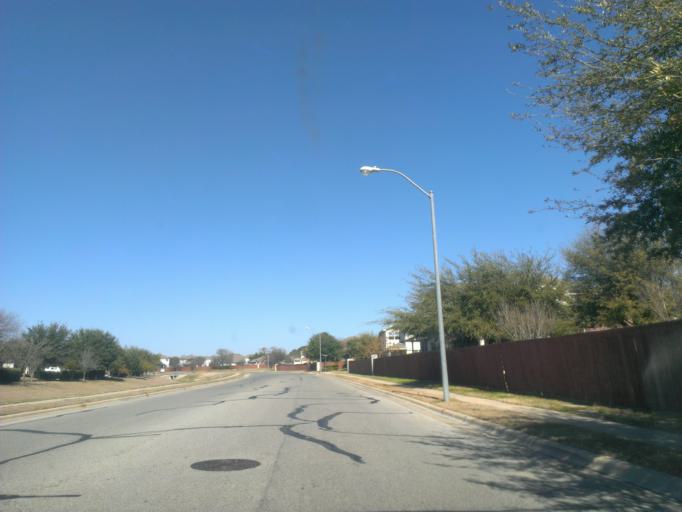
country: US
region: Texas
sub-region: Williamson County
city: Round Rock
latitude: 30.5318
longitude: -97.6197
